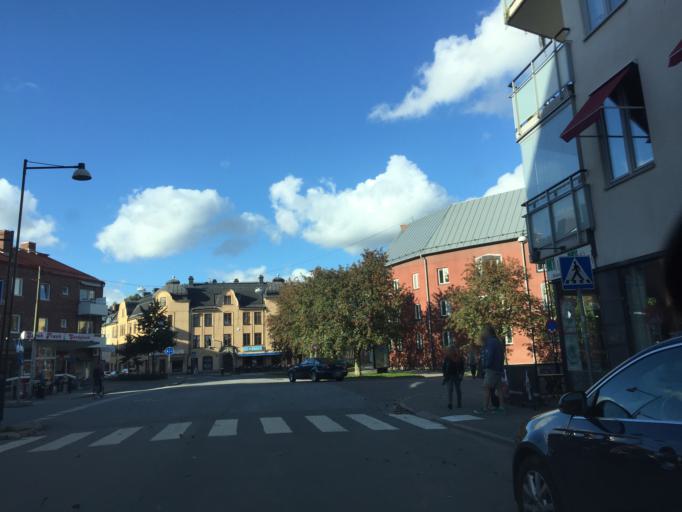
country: SE
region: OErebro
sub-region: Orebro Kommun
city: Orebro
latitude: 59.2769
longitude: 15.2049
